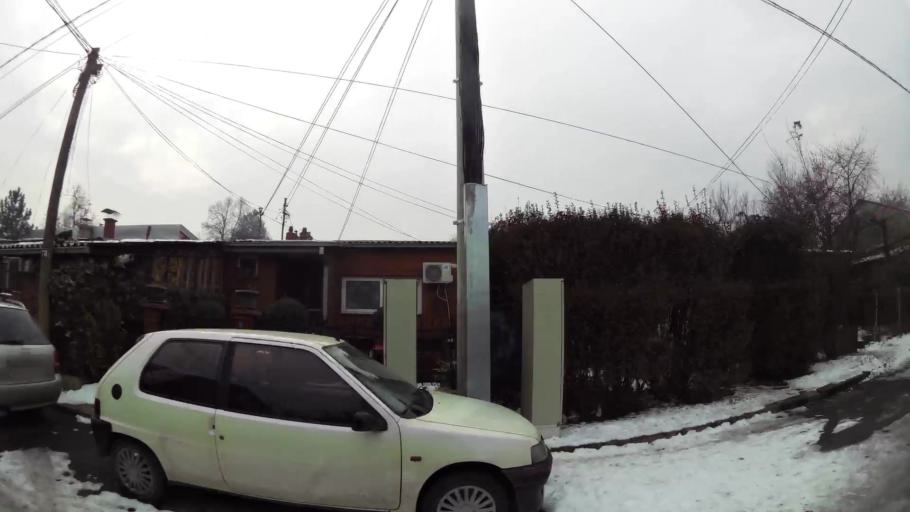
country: MK
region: Kisela Voda
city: Kisela Voda
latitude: 41.9993
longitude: 21.4910
